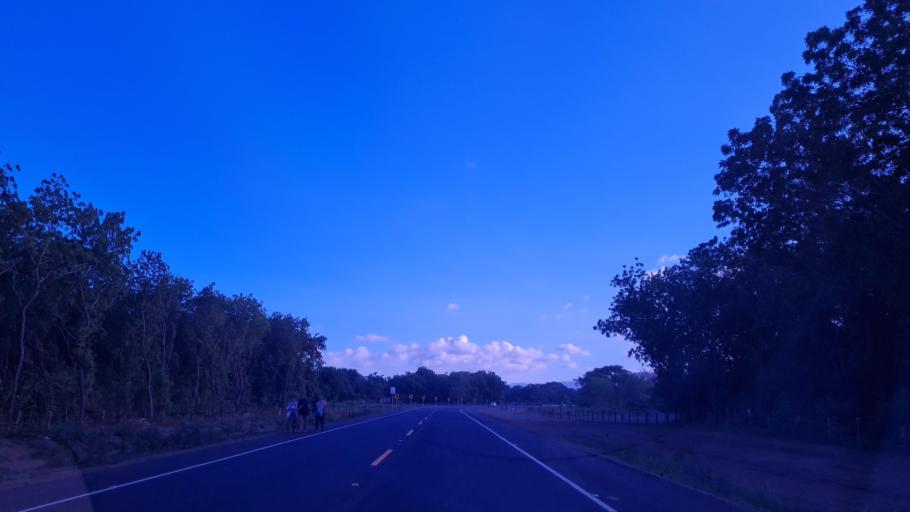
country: NI
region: Masaya
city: Ticuantepe
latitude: 12.0940
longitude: -86.1612
